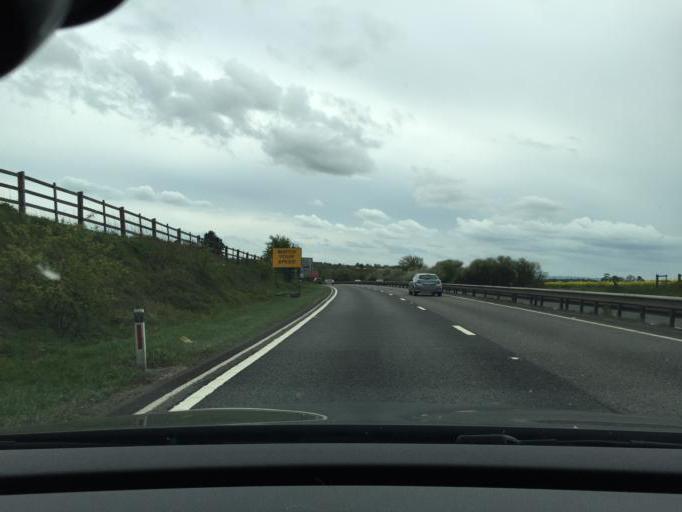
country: GB
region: England
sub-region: West Berkshire
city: Hermitage
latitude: 51.5065
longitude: -1.2937
